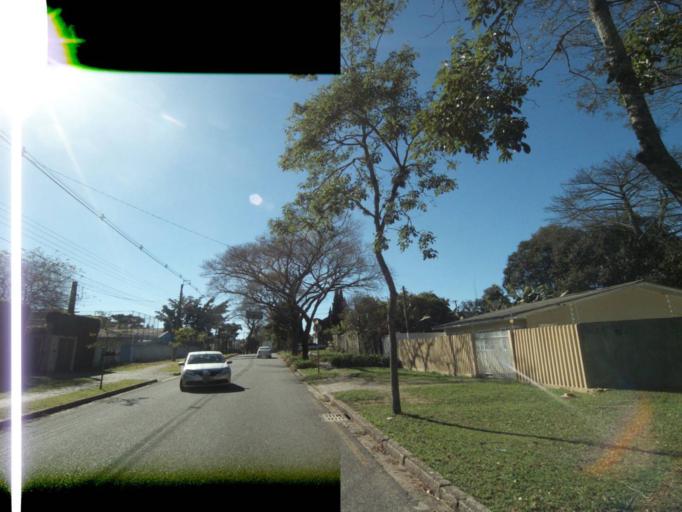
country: BR
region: Parana
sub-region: Curitiba
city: Curitiba
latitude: -25.4210
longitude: -49.2458
